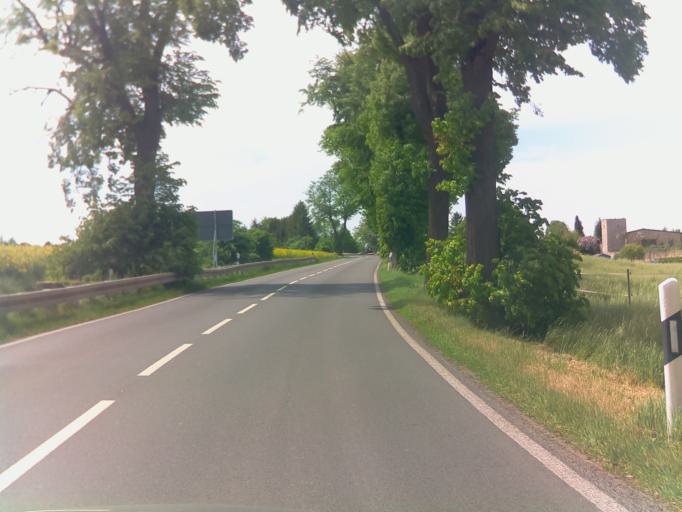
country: DE
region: Saxony-Anhalt
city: Kroppenstedt
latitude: 51.9396
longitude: 11.3140
